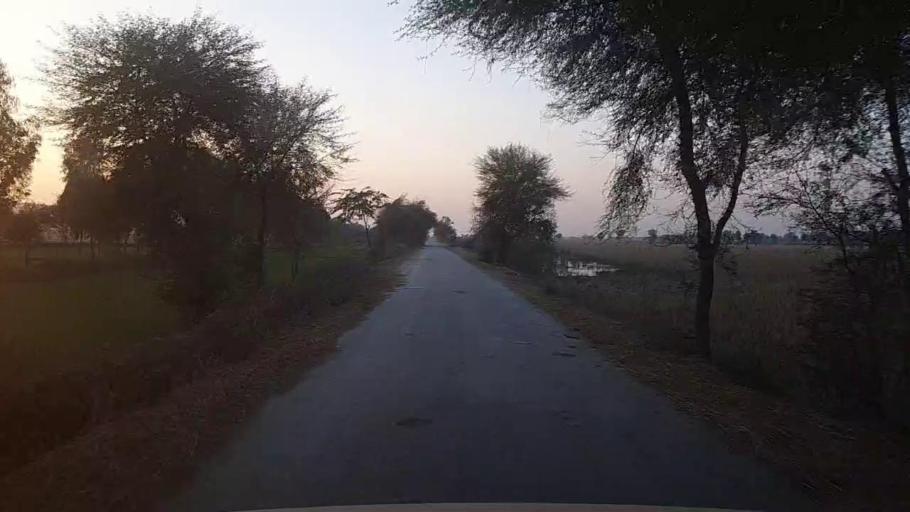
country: PK
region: Sindh
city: Khairpur Nathan Shah
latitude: 27.1579
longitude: 67.7150
